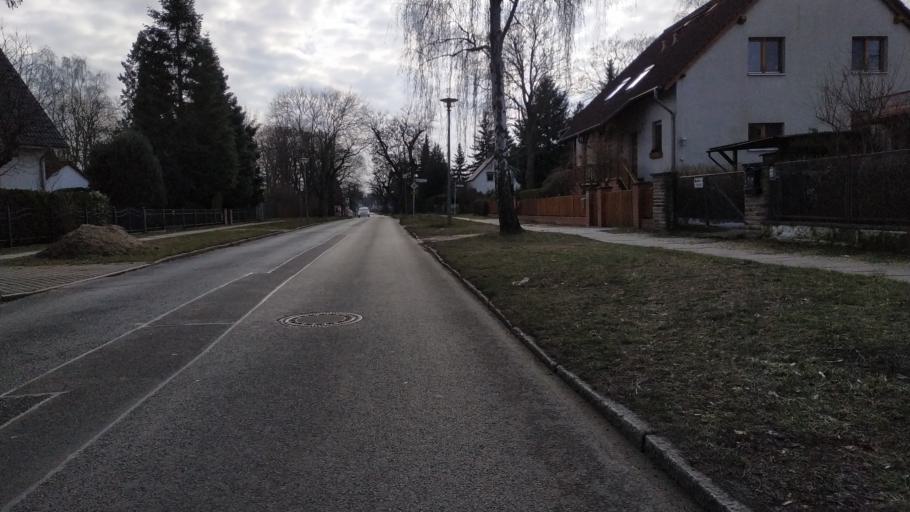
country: DE
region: Berlin
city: Mahlsdorf
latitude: 52.5196
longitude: 13.6066
